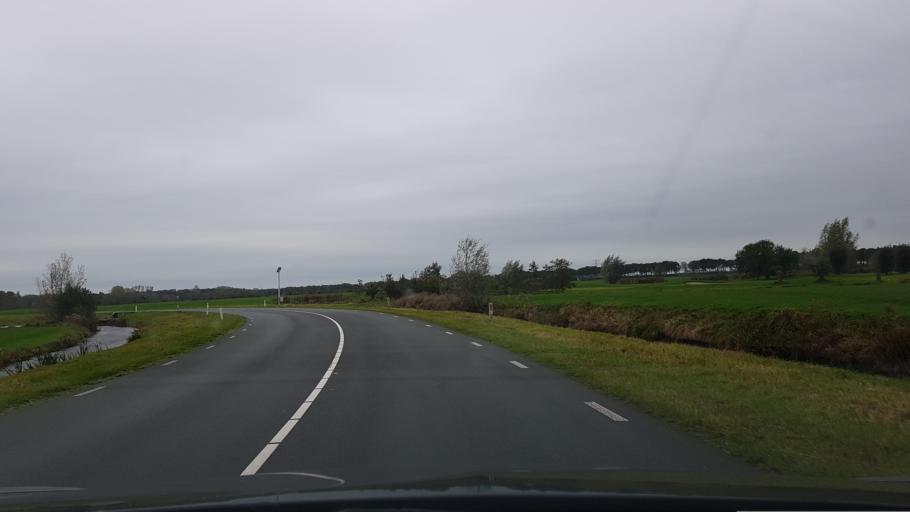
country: NL
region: Utrecht
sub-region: Stichtse Vecht
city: Vreeland
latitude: 52.2117
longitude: 5.0124
